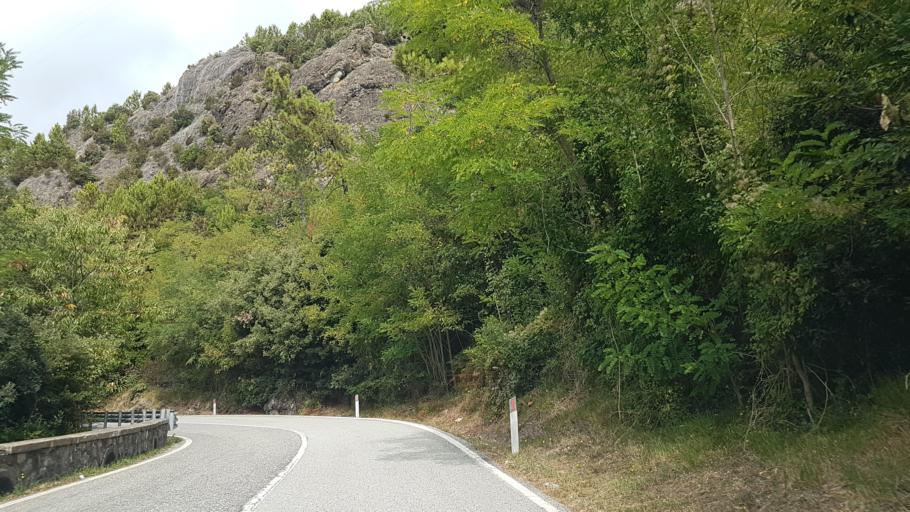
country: IT
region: Liguria
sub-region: Provincia di La Spezia
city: Framura
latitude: 44.2465
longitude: 9.5773
